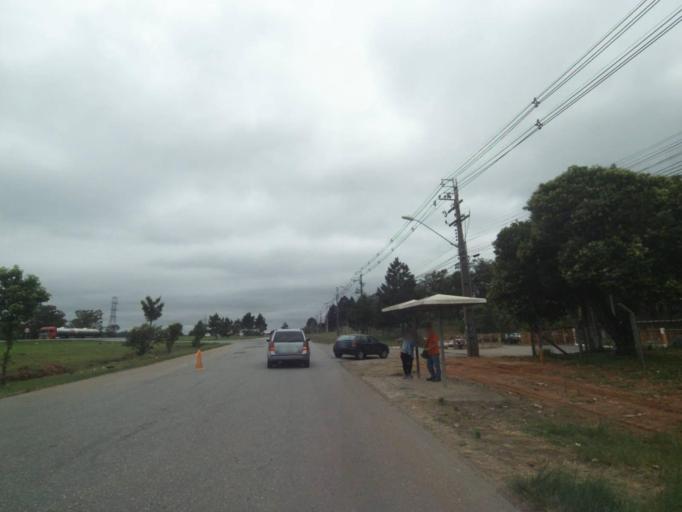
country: BR
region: Parana
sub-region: Araucaria
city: Araucaria
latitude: -25.5494
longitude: -49.3244
